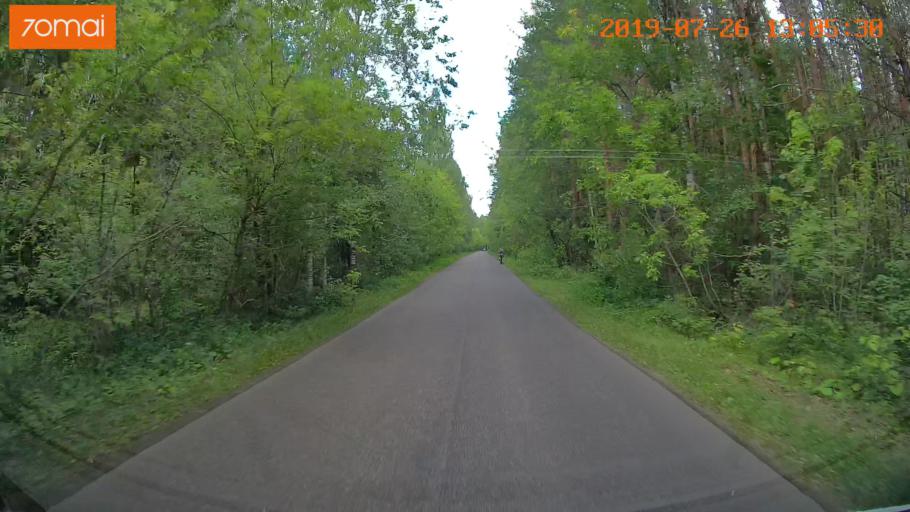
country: RU
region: Ivanovo
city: Bogorodskoye
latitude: 57.0630
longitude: 41.0361
